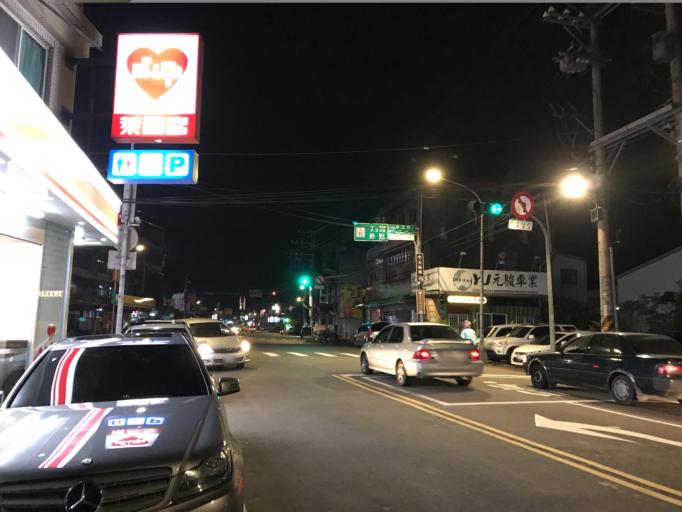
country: TW
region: Taiwan
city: Daxi
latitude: 24.9196
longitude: 121.3668
